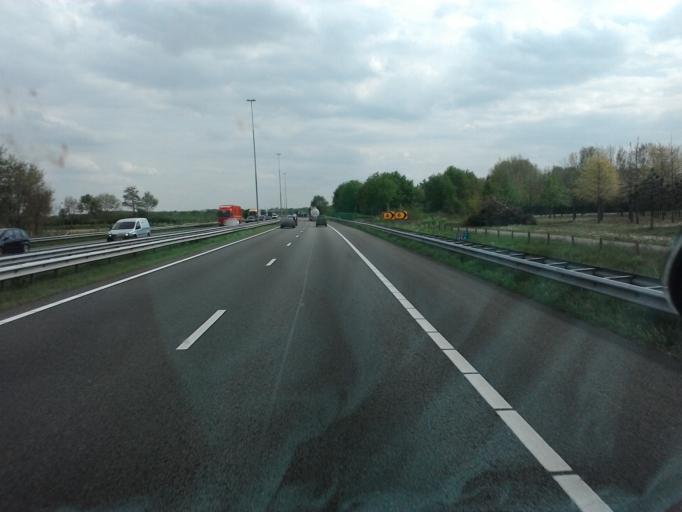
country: NL
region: North Brabant
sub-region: Gemeente Cuijk
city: Cuijk
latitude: 51.7070
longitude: 5.8745
